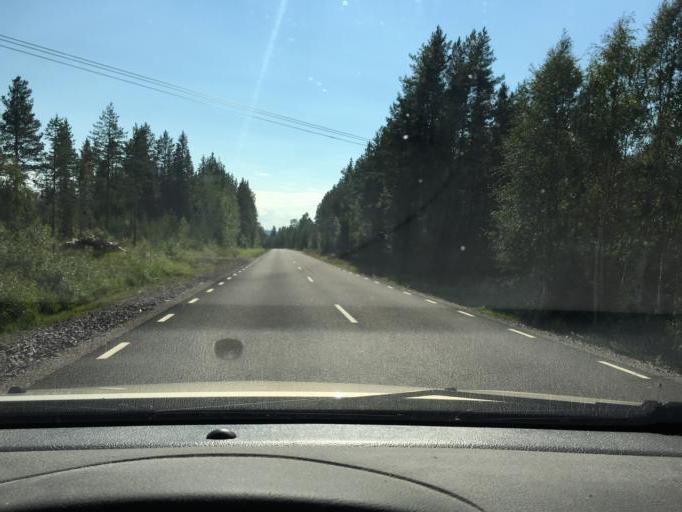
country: SE
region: Norrbotten
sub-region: Lulea Kommun
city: Ranea
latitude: 66.0438
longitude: 22.1892
